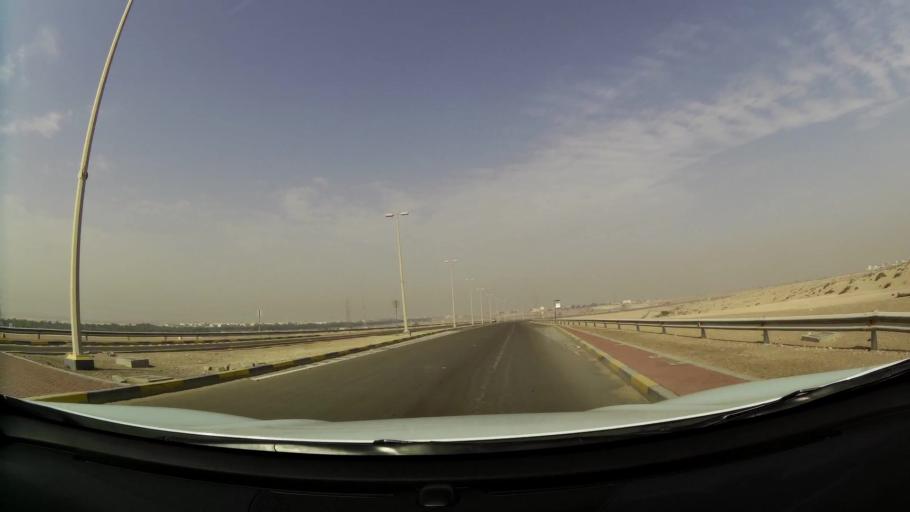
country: AE
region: Abu Dhabi
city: Abu Dhabi
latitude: 24.2648
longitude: 54.6888
